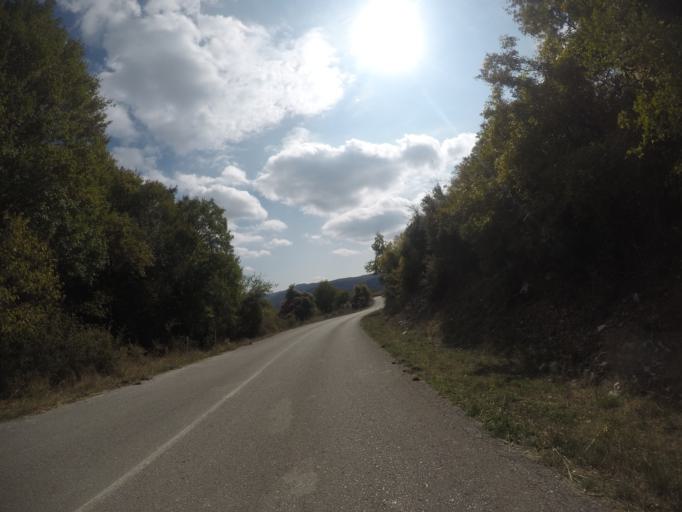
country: GR
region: Epirus
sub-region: Nomos Ioanninon
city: Kalpaki
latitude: 39.8974
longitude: 20.6706
